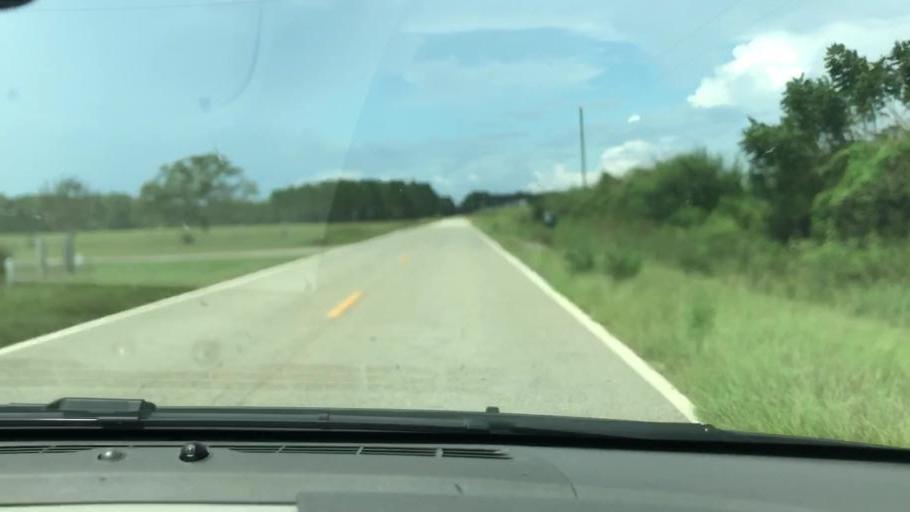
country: US
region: Georgia
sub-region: Seminole County
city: Donalsonville
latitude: 31.1406
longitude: -84.9951
